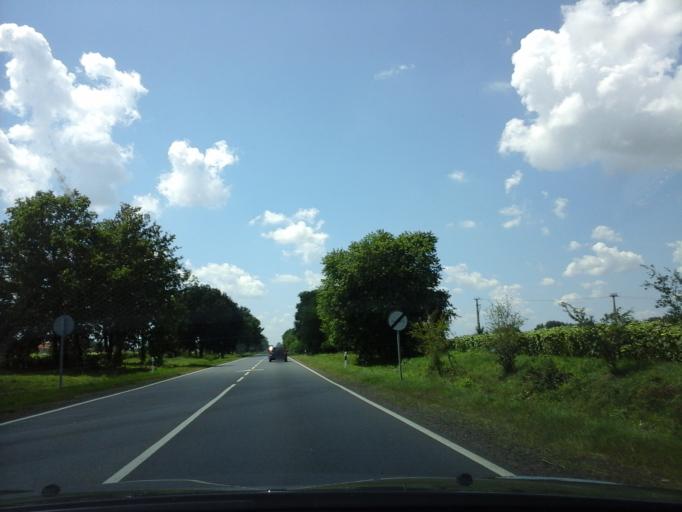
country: HU
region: Hajdu-Bihar
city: Ebes
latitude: 47.4809
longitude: 21.4982
